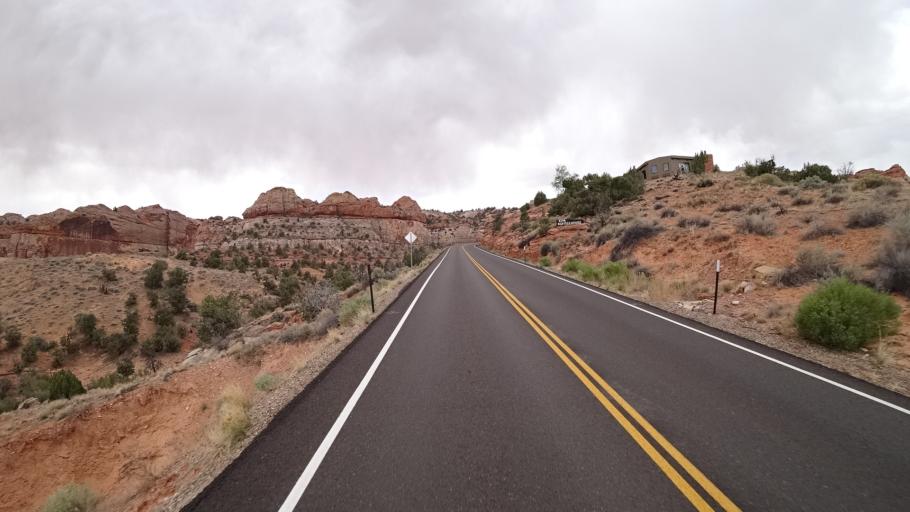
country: US
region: Utah
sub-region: Wayne County
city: Loa
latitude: 37.7722
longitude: -111.4161
